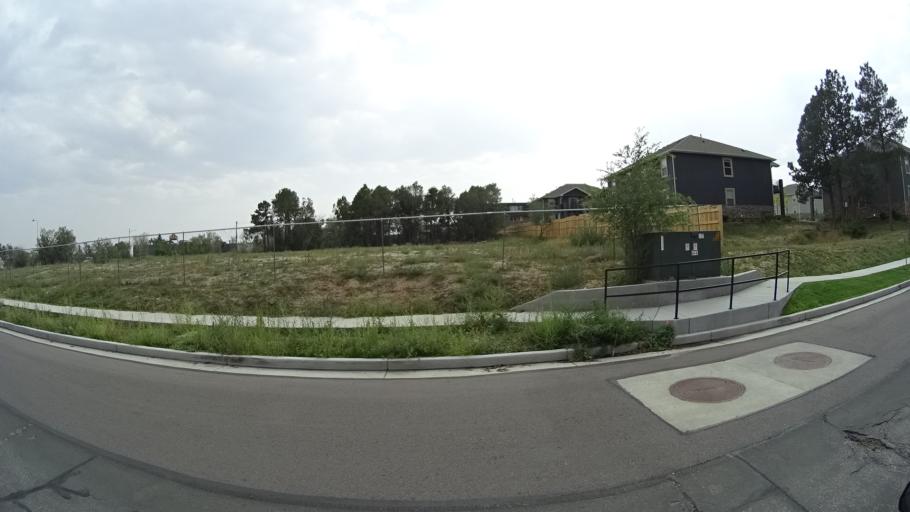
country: US
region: Colorado
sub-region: El Paso County
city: Colorado Springs
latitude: 38.8507
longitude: -104.7768
